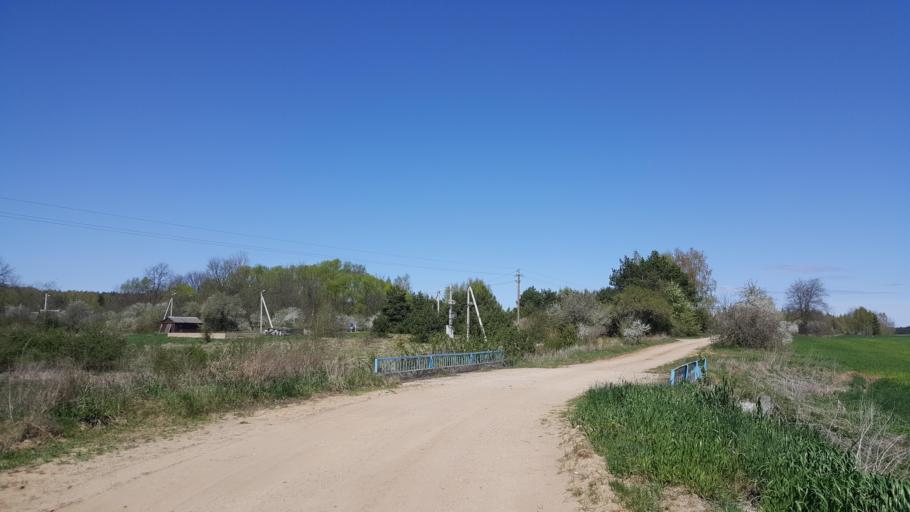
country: BY
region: Brest
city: Charnawchytsy
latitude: 52.3282
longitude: 23.6959
